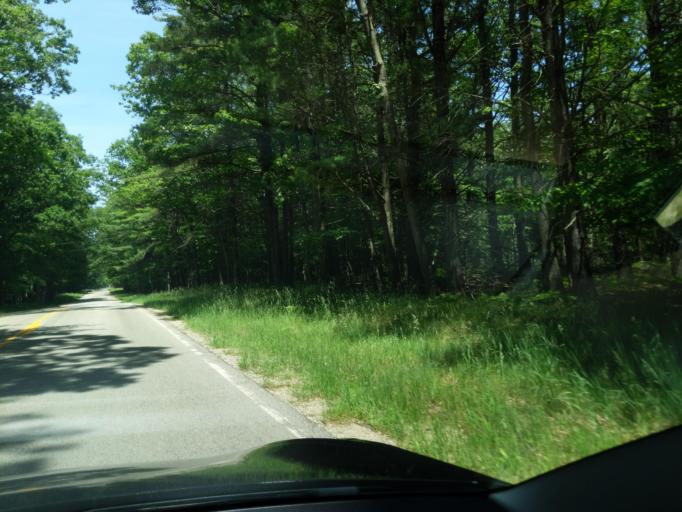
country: US
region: Michigan
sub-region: Muskegon County
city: Montague
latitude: 43.3936
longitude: -86.4162
